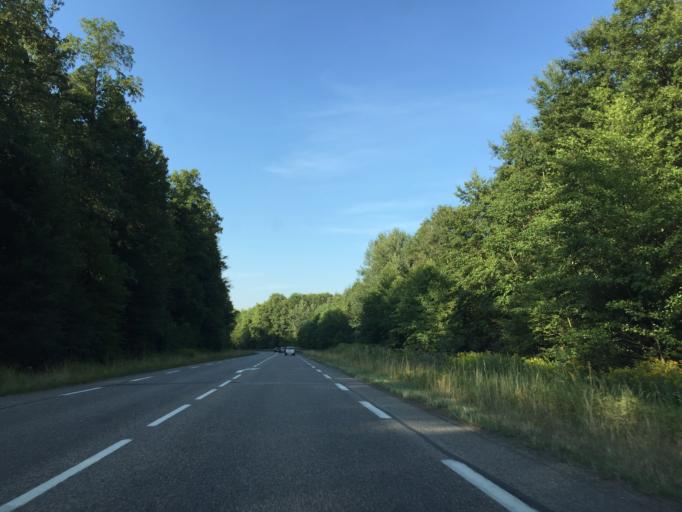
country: FR
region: Alsace
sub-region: Departement du Bas-Rhin
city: Walbourg
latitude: 48.8627
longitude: 7.8227
